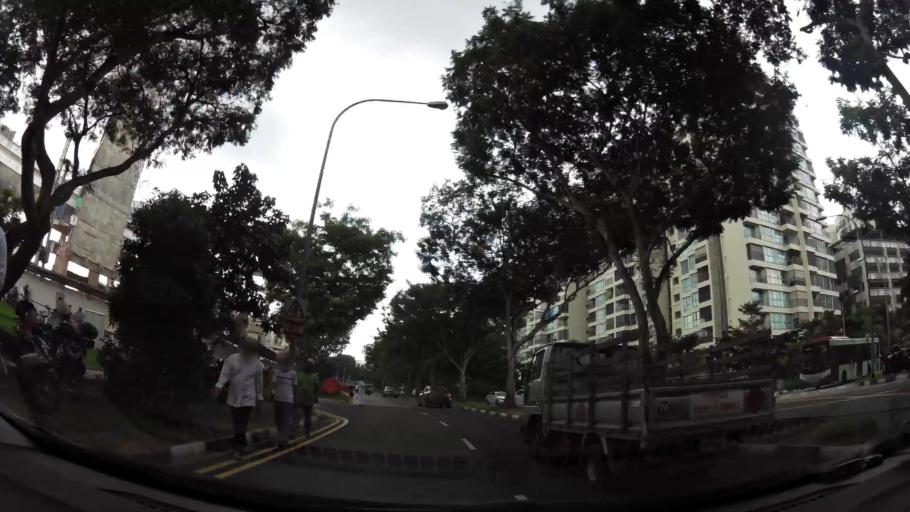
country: SG
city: Singapore
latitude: 1.3558
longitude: 103.9404
